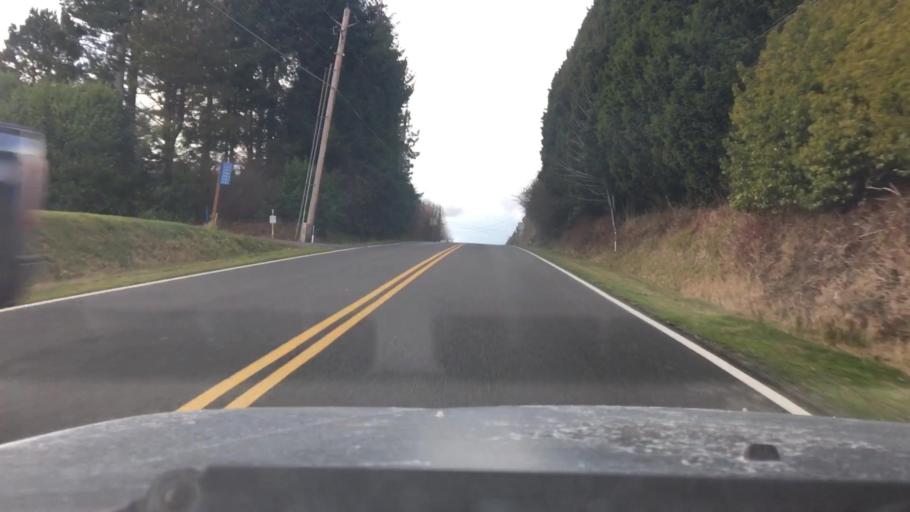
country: US
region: Washington
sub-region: Whatcom County
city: Ferndale
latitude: 48.8484
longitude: -122.6210
